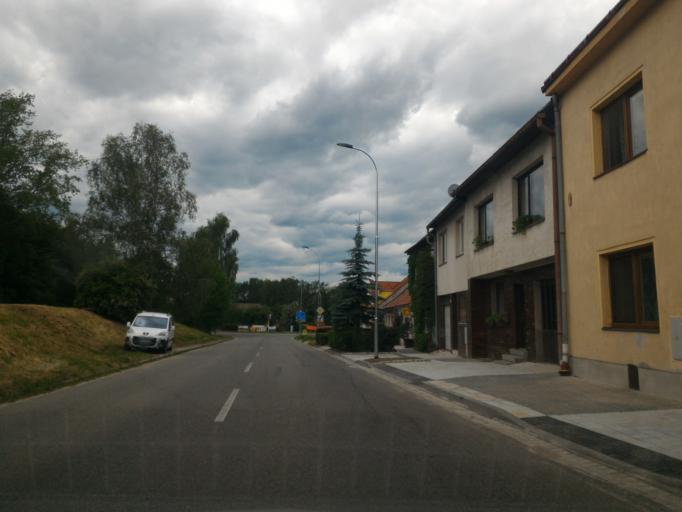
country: CZ
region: Vysocina
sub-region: Okres Jihlava
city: Telc
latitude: 49.1899
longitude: 15.4509
